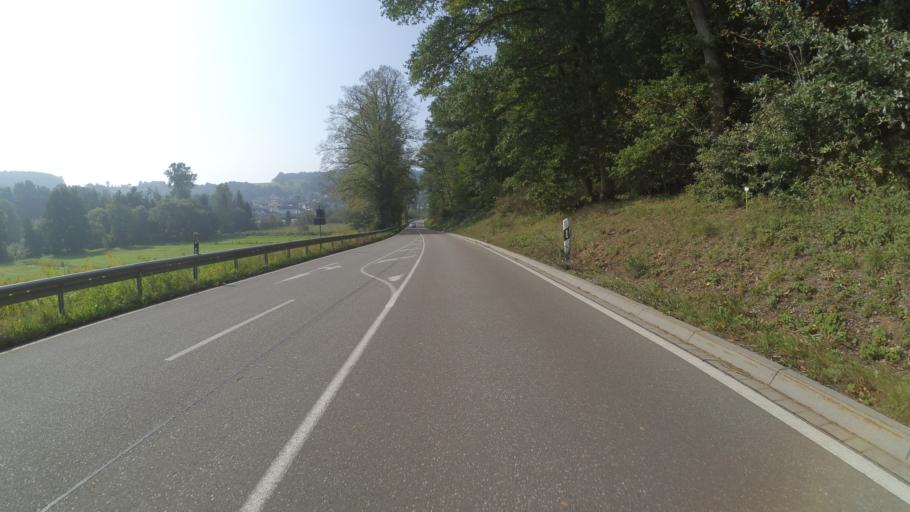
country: DE
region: Rheinland-Pfalz
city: Massweiler
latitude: 49.2471
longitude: 7.5265
